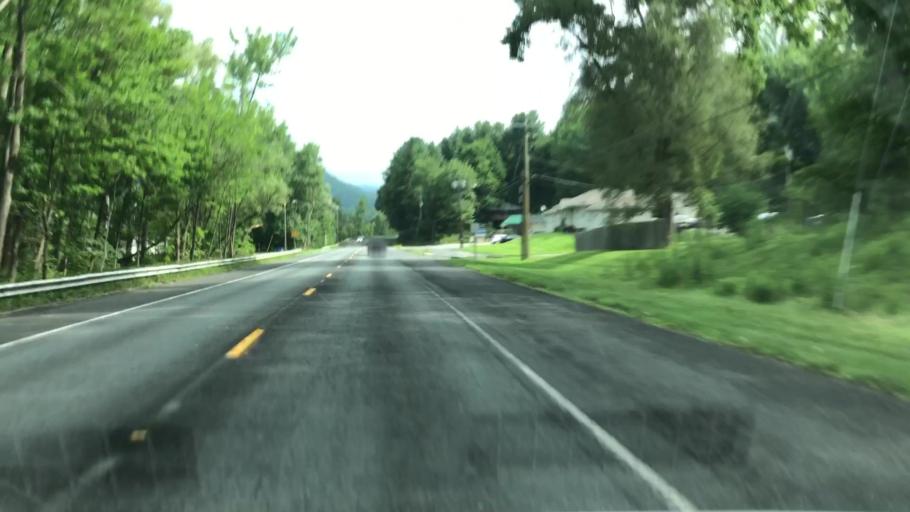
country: US
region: Massachusetts
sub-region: Berkshire County
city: Lanesborough
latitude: 42.5248
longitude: -73.1917
